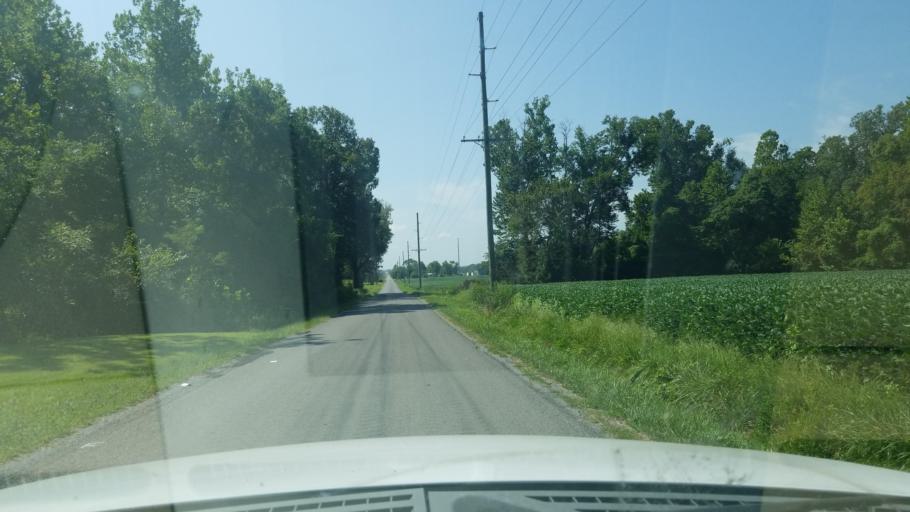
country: US
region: Illinois
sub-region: Saline County
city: Harrisburg
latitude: 37.8486
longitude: -88.6517
